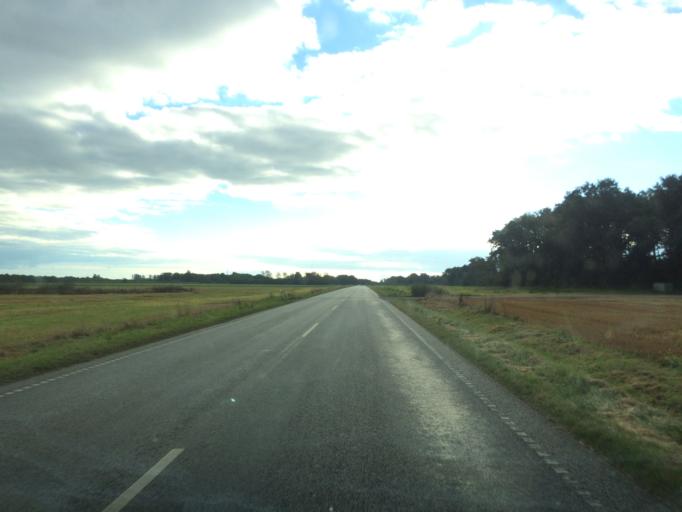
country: DK
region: Central Jutland
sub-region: Herning Kommune
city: Kibaek
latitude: 55.9470
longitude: 8.7569
